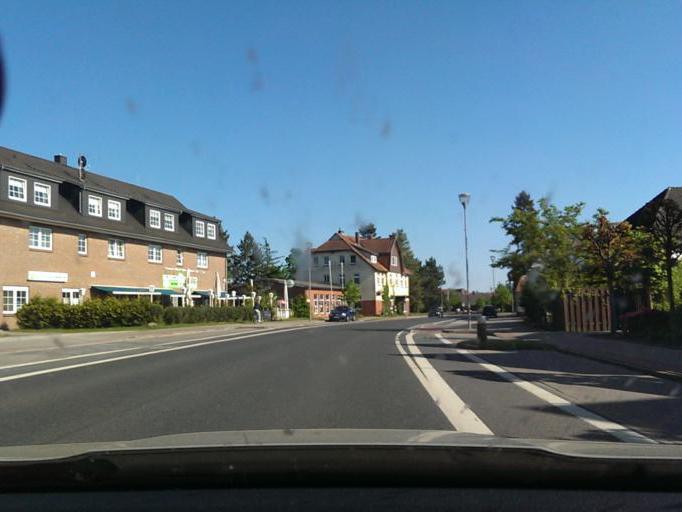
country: DE
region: Lower Saxony
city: Wietze
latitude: 52.6524
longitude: 9.8445
